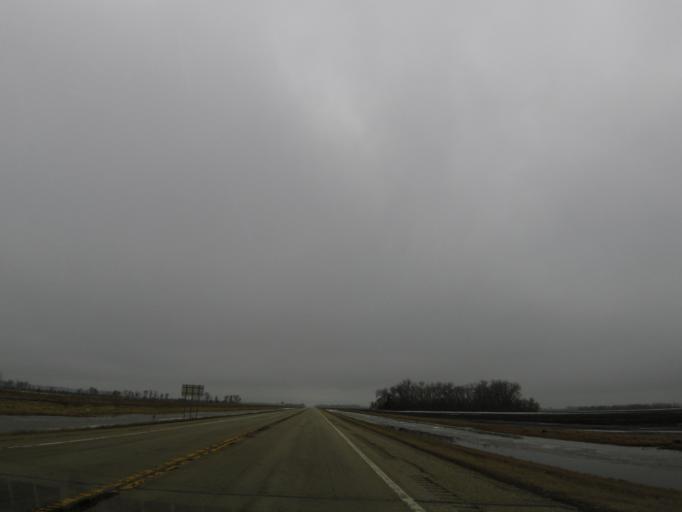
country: US
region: North Dakota
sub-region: Walsh County
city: Grafton
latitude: 48.5703
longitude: -97.4480
